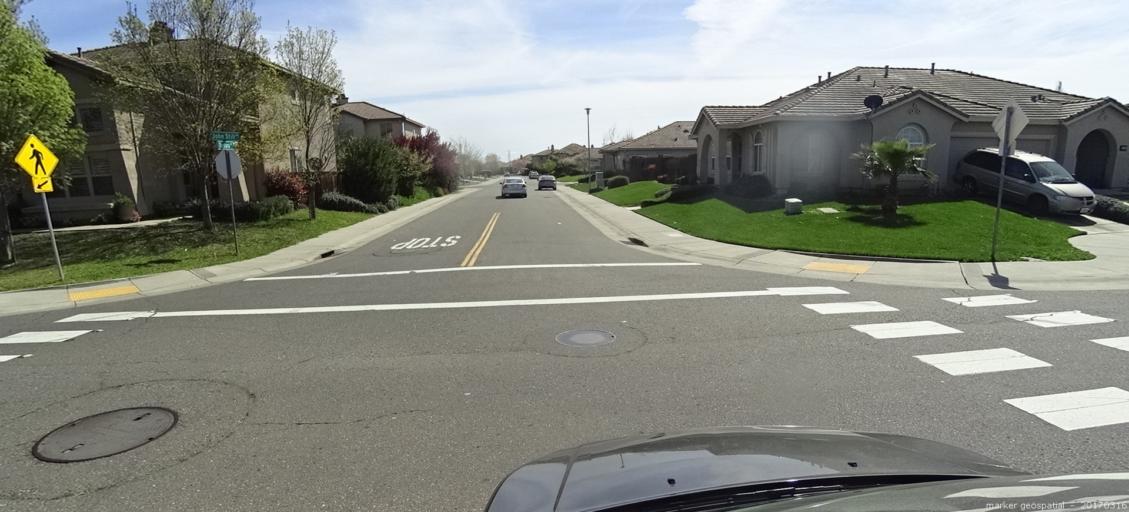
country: US
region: California
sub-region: Sacramento County
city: Parkway
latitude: 38.4750
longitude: -121.4926
